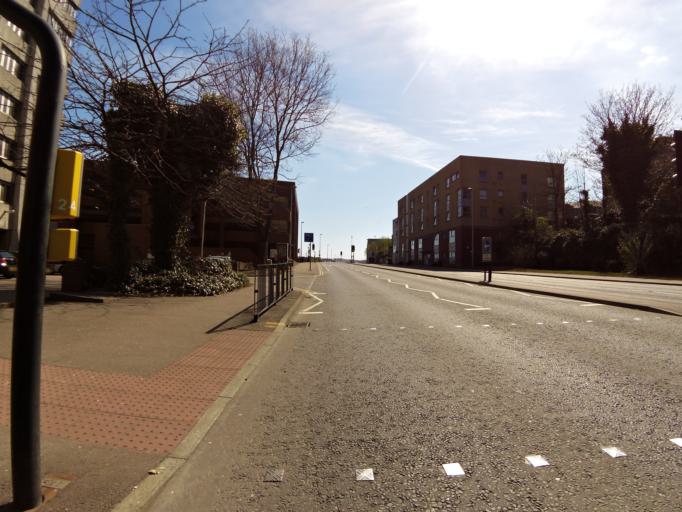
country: GB
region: Scotland
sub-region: Aberdeen City
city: Aberdeen
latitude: 57.1433
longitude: -2.1000
